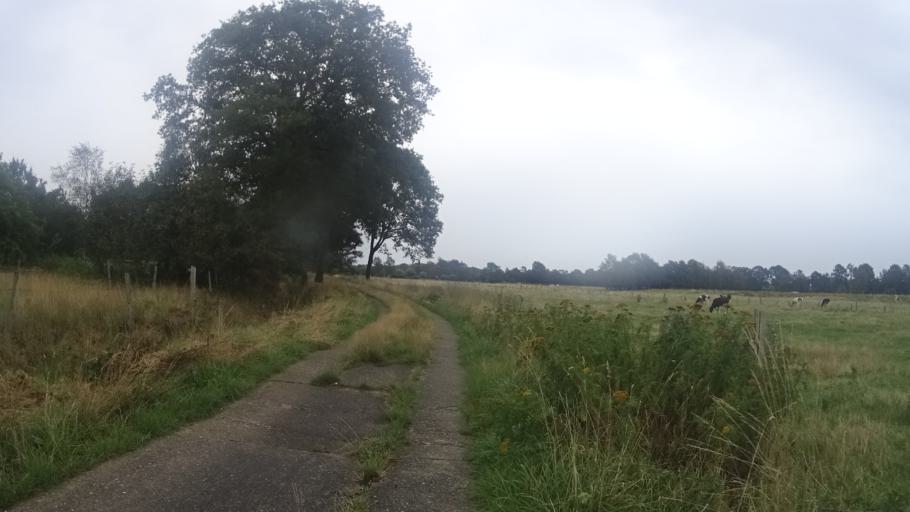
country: DE
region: Schleswig-Holstein
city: Heede
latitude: 53.7596
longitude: 9.7998
